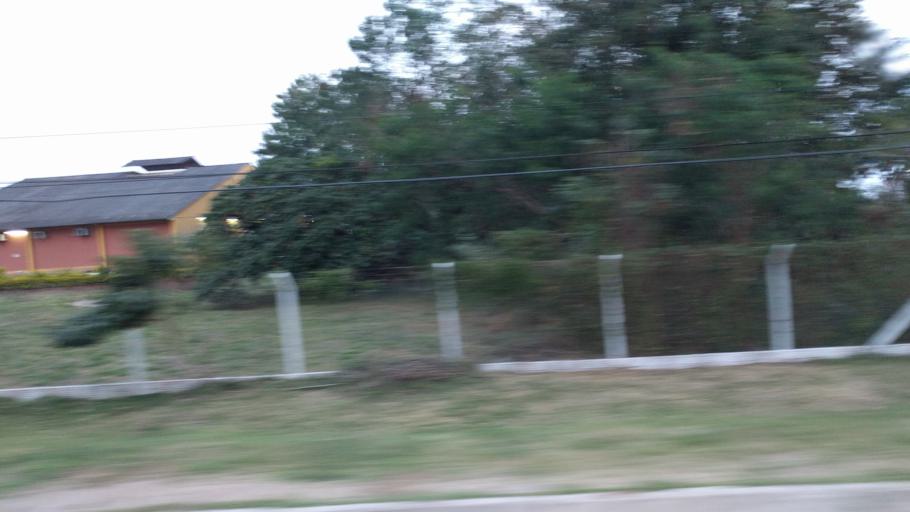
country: BO
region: Santa Cruz
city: Santa Rita
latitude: -17.8912
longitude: -63.3179
